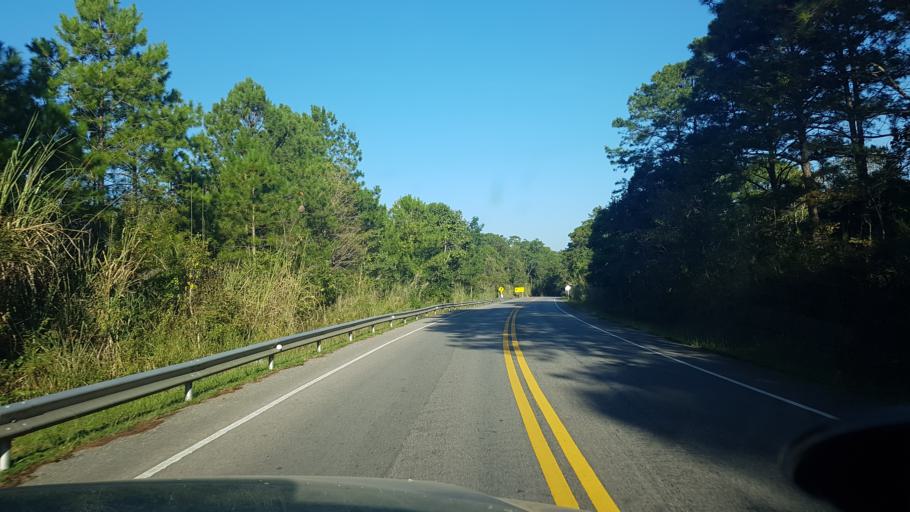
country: TH
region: Phetchabun
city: Nam Nao
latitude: 16.7314
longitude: 101.5536
